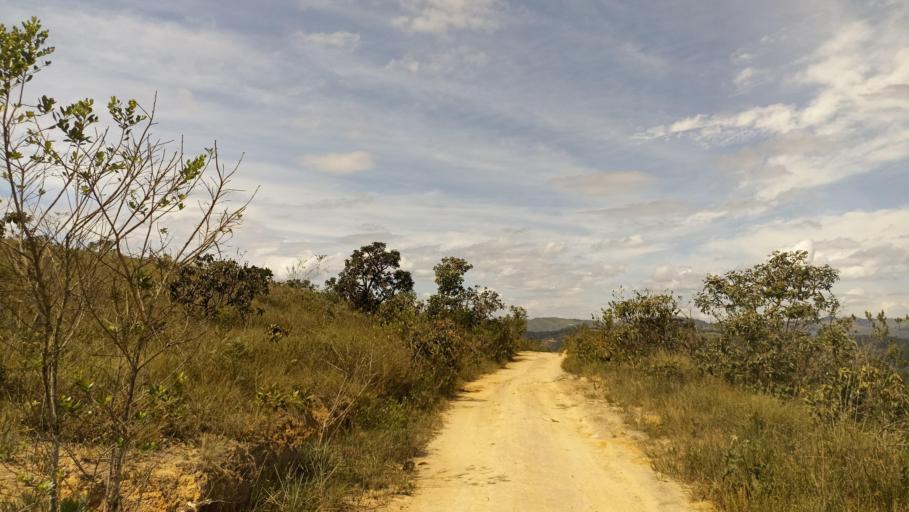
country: BR
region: Minas Gerais
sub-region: Itabirito
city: Itabirito
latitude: -20.3444
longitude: -43.7261
